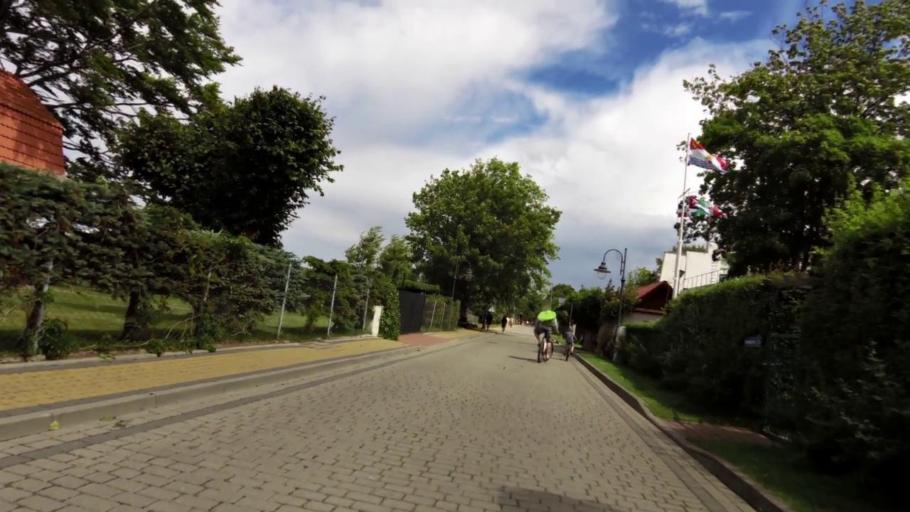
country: PL
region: West Pomeranian Voivodeship
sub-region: Powiat slawienski
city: Darlowo
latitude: 54.5394
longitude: 16.5297
